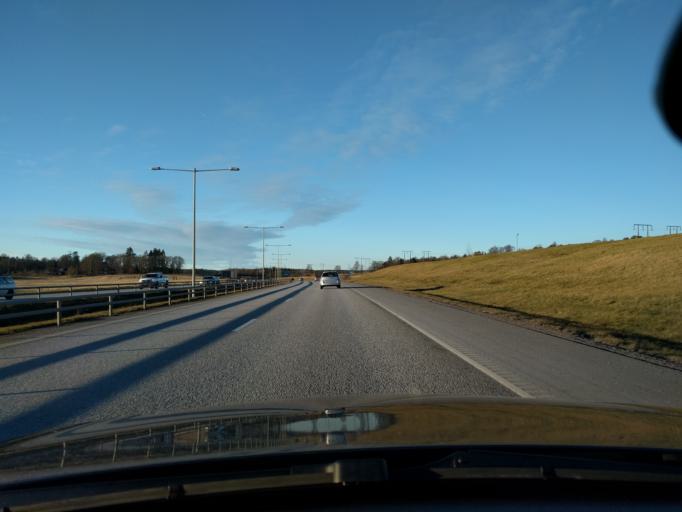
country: SE
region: Stockholm
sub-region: Taby Kommun
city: Taby
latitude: 59.4755
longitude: 18.0306
